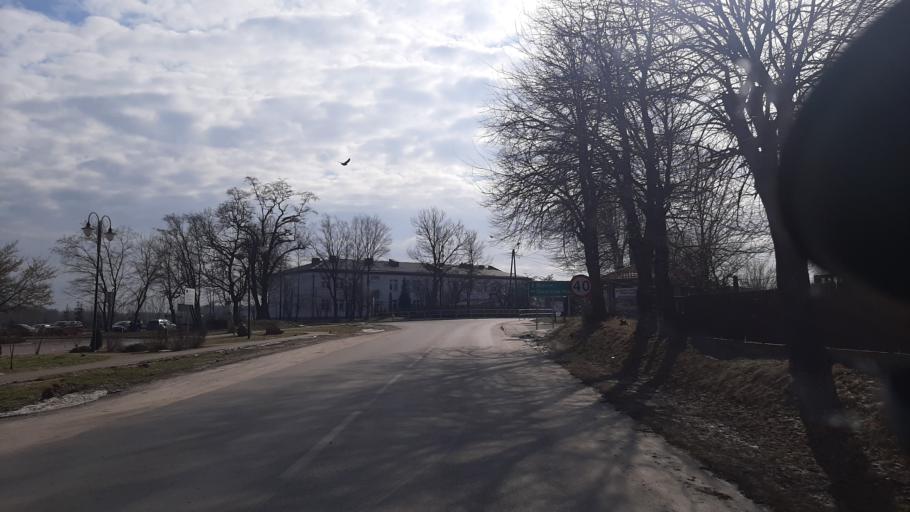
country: PL
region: Lublin Voivodeship
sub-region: Powiat lubartowski
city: Uscimow Stary
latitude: 51.4726
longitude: 22.9424
